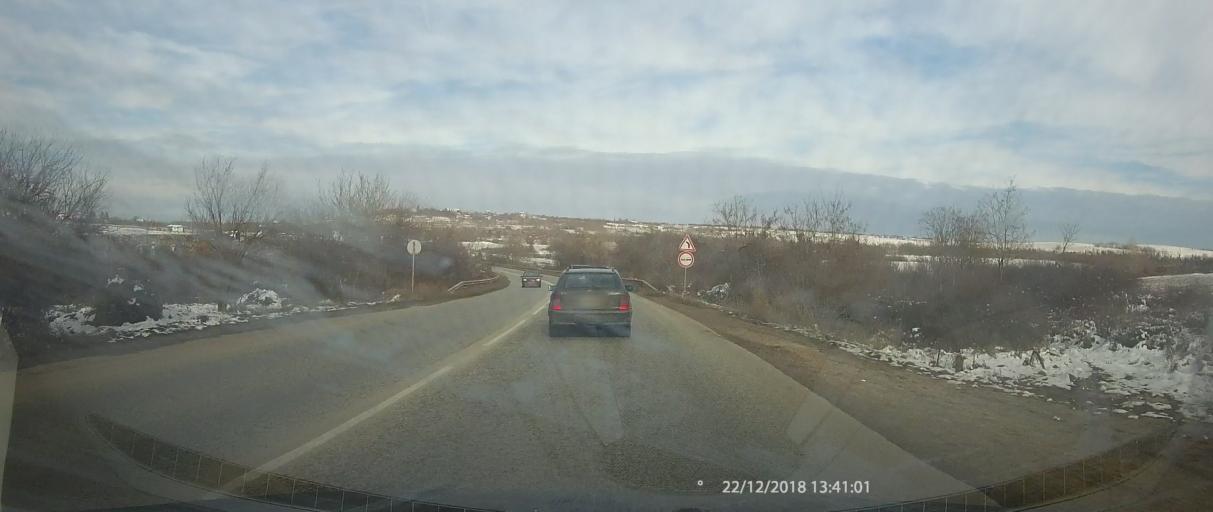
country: BG
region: Lovech
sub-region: Obshtina Lukovit
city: Lukovit
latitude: 43.1835
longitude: 24.1596
